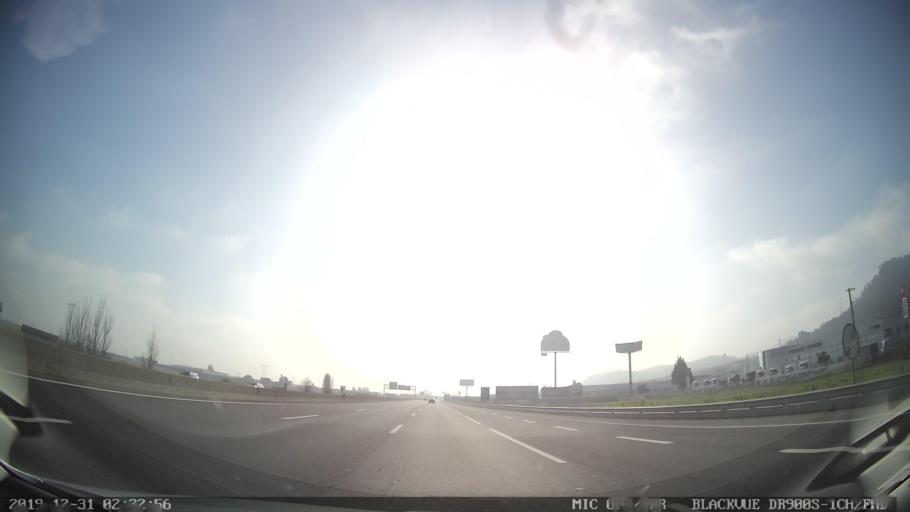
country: PT
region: Lisbon
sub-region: Vila Franca de Xira
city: Castanheira do Ribatejo
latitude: 39.0024
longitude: -8.9675
